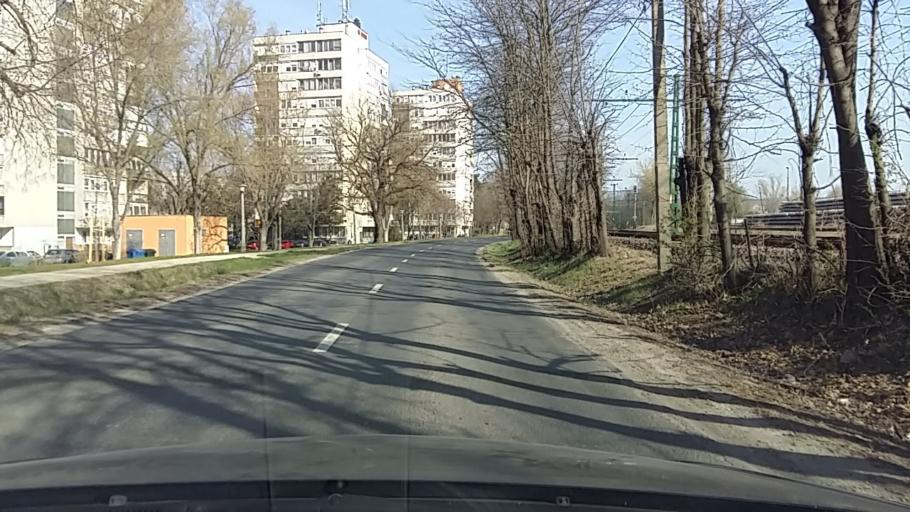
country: HU
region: Pest
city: Godollo
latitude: 47.5954
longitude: 19.3569
